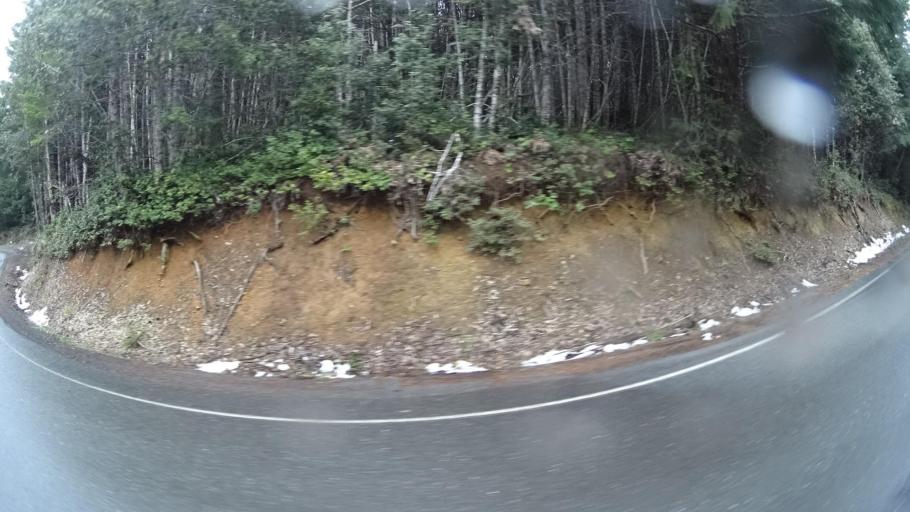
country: US
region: California
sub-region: Humboldt County
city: Willow Creek
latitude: 41.1691
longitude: -123.8145
